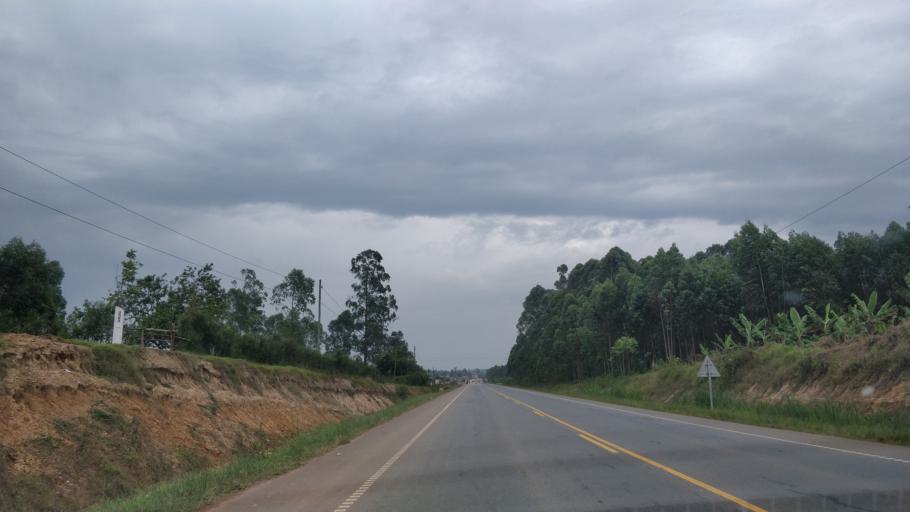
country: UG
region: Western Region
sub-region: Sheema District
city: Kibingo
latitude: -0.6669
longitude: 30.4460
